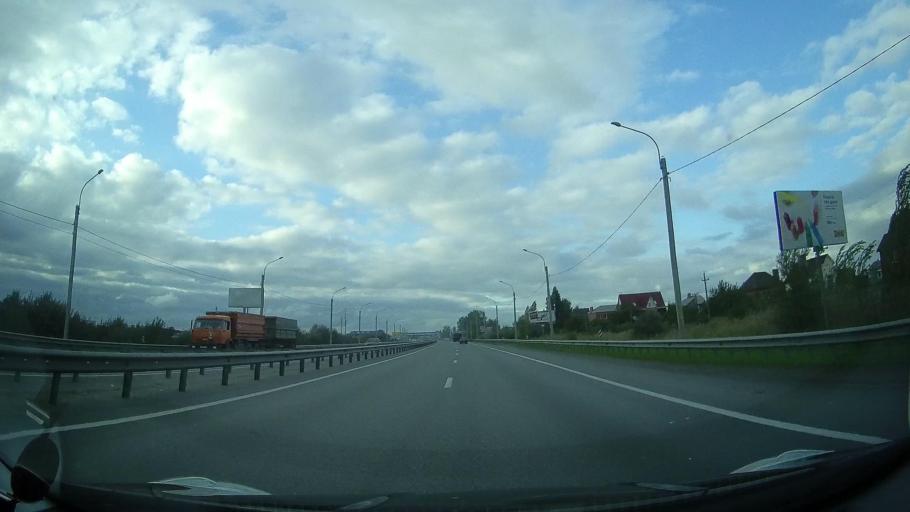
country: RU
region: Rostov
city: Bataysk
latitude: 47.1500
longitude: 39.7732
